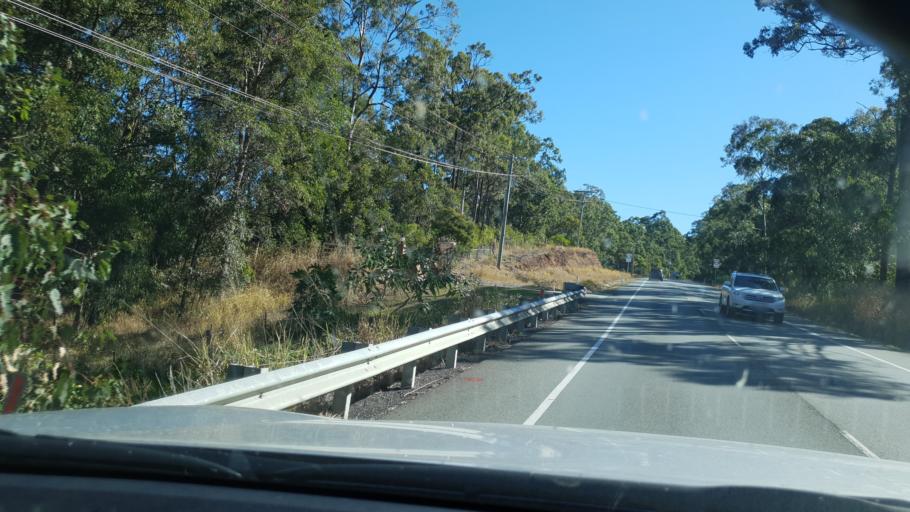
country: AU
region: Queensland
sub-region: Moreton Bay
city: Strathpine
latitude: -27.3297
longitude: 152.9401
